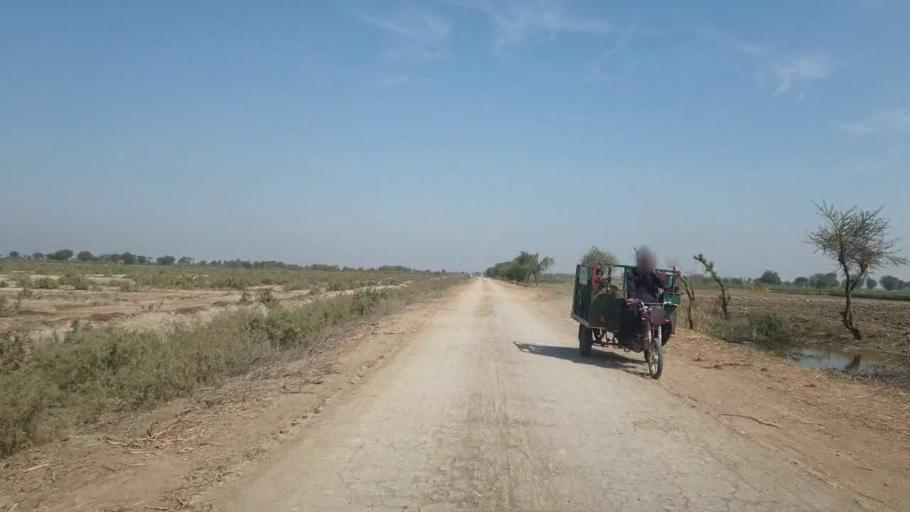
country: PK
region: Sindh
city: Samaro
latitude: 25.3285
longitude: 69.2433
